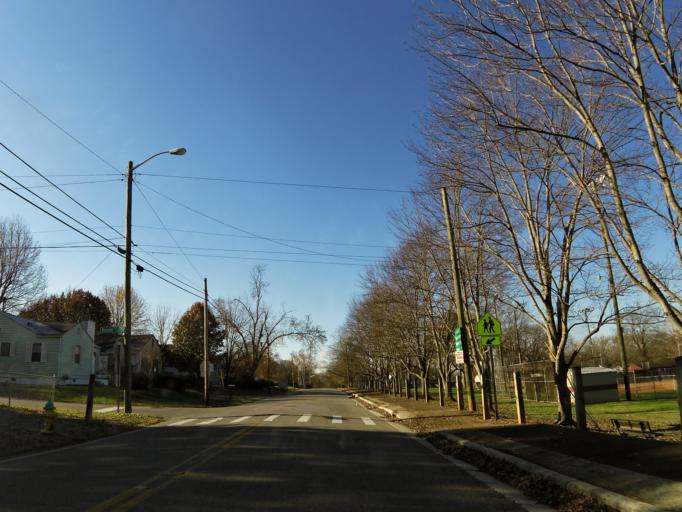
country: US
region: Tennessee
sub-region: Knox County
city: Knoxville
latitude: 35.9944
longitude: -83.9304
